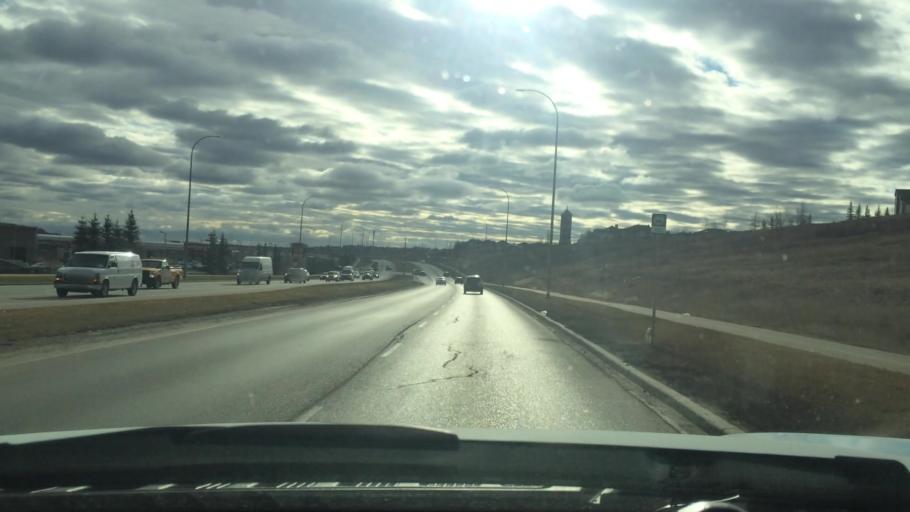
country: CA
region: Alberta
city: Calgary
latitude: 51.1654
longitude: -114.1301
